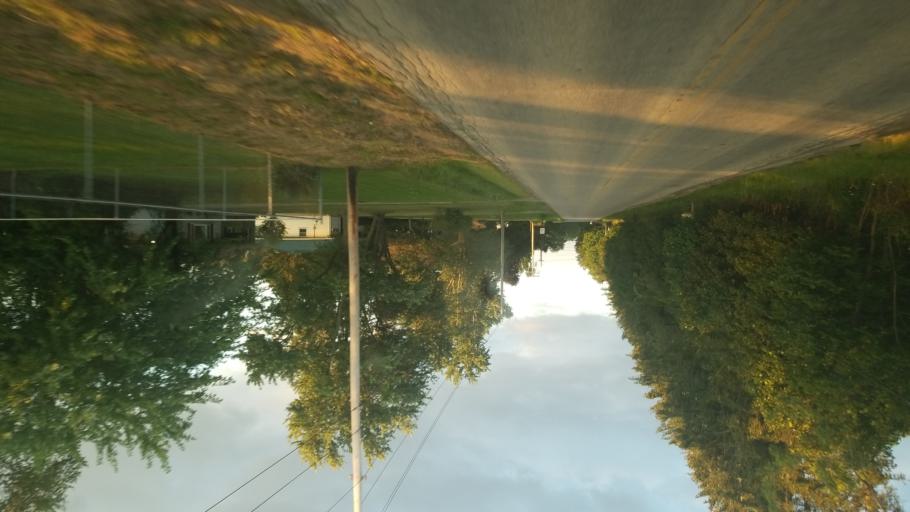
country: US
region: Ohio
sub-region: Richland County
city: Mansfield
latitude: 40.8075
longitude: -82.5401
